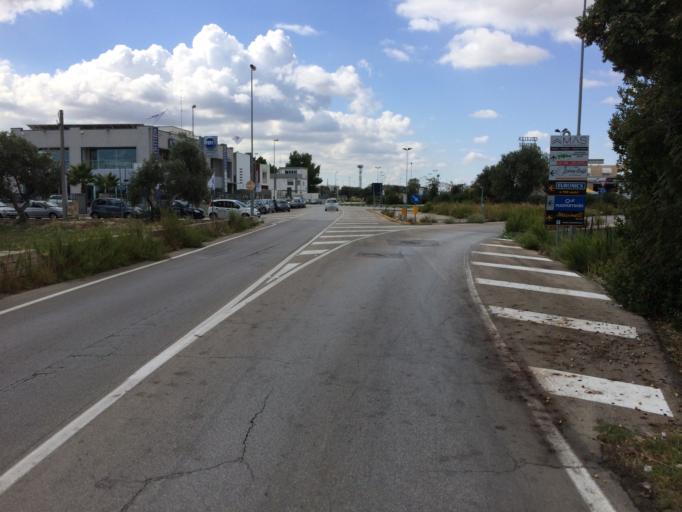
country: IT
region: Apulia
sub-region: Provincia di Bari
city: Bari
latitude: 41.1029
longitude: 16.8363
